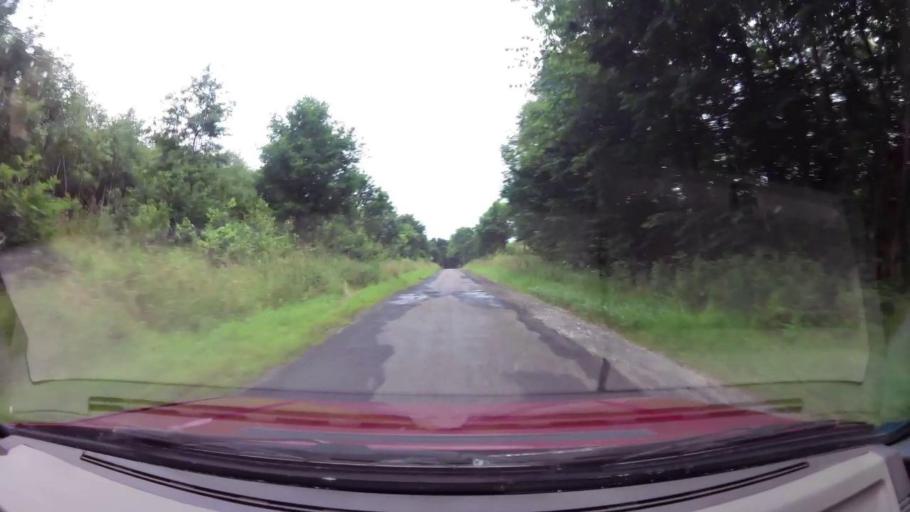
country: PL
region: West Pomeranian Voivodeship
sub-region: Powiat swidwinski
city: Rabino
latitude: 53.9282
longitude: 15.9650
